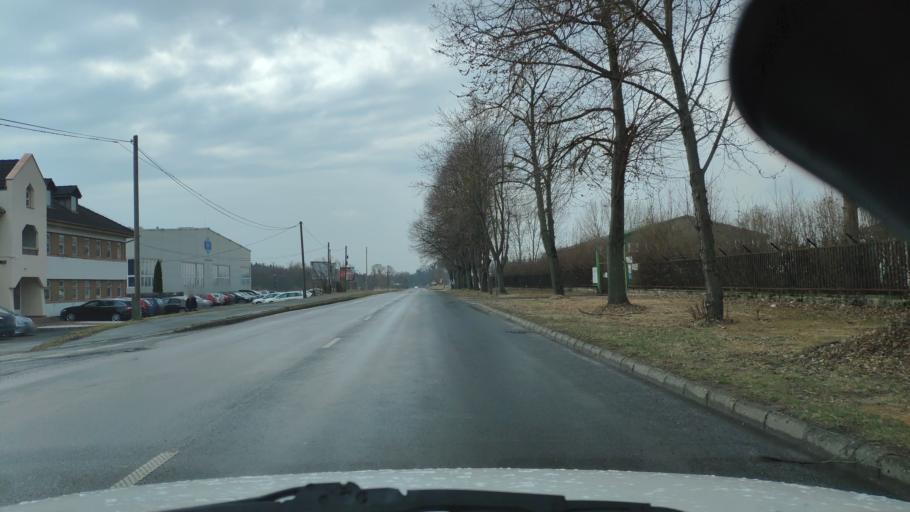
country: HU
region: Zala
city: Nagykanizsa
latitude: 46.4237
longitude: 16.9860
